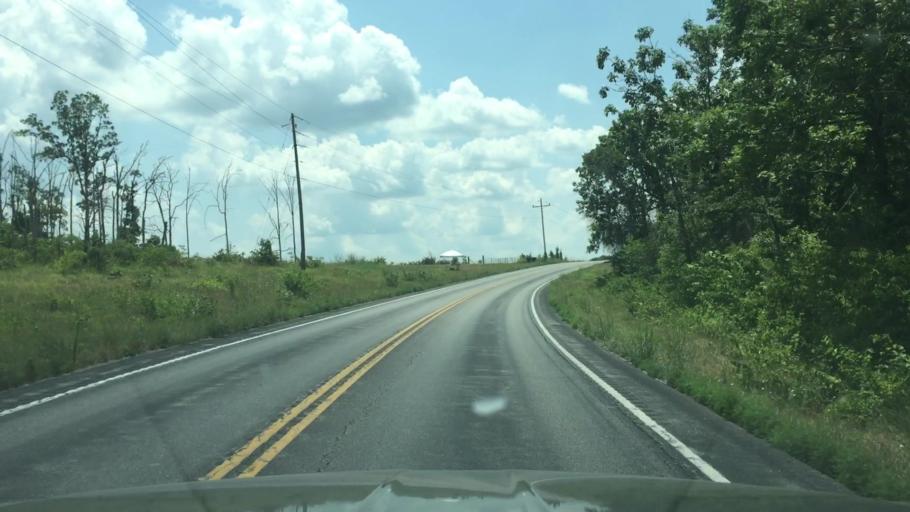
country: US
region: Missouri
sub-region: Miller County
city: Tuscumbia
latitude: 38.1110
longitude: -92.5038
